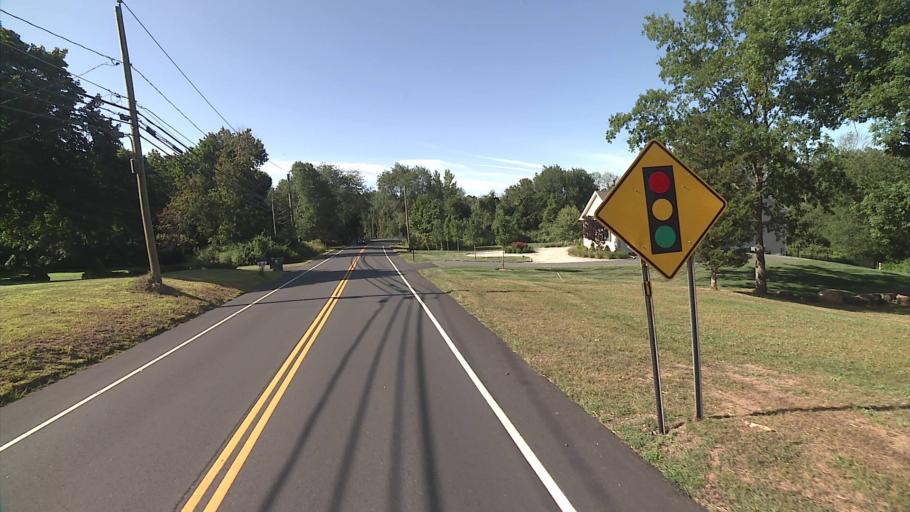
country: US
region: Connecticut
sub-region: New Haven County
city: Cheshire Village
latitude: 41.5024
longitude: -72.8778
